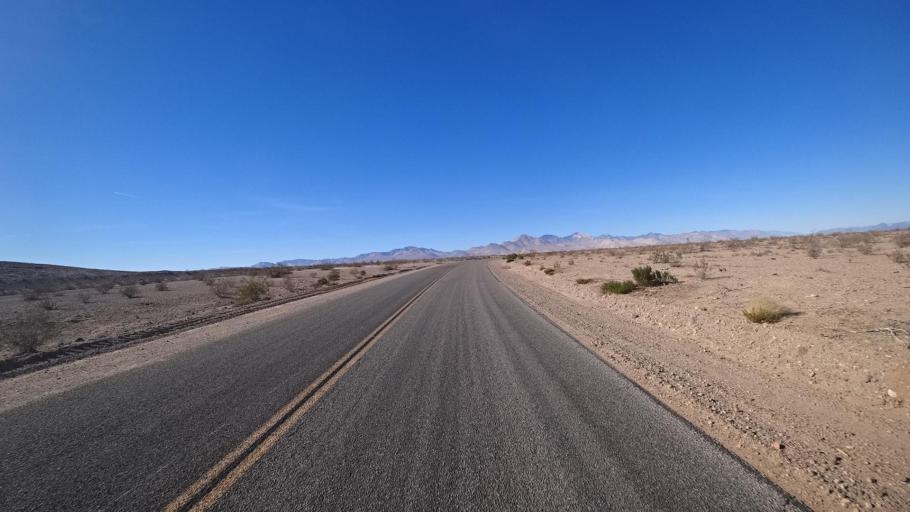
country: US
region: California
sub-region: Kern County
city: China Lake Acres
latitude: 35.5620
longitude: -117.7737
